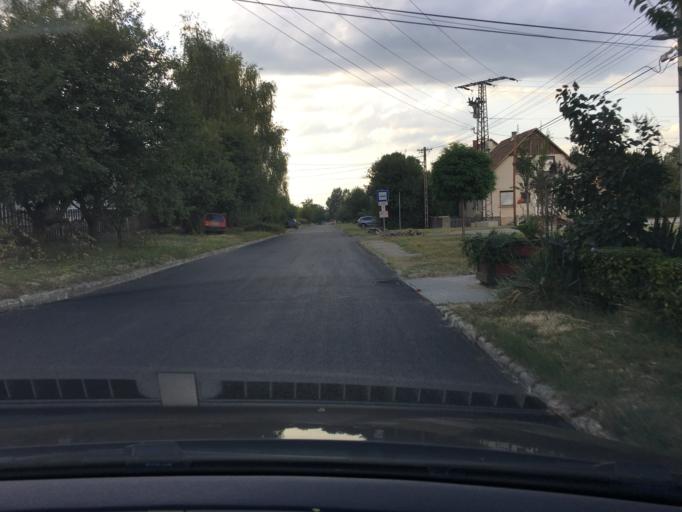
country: HU
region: Pest
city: Veresegyhaz
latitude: 47.6520
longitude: 19.2967
